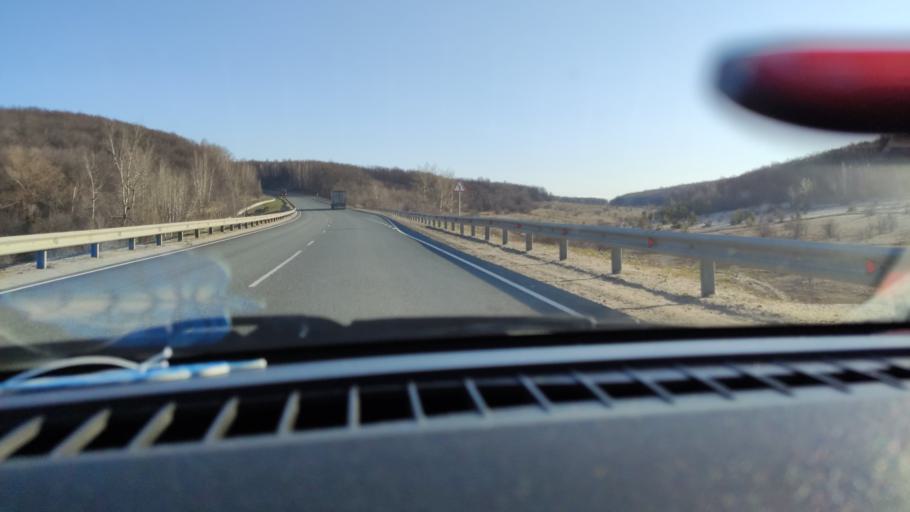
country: RU
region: Saratov
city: Alekseyevka
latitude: 52.4113
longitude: 48.0050
